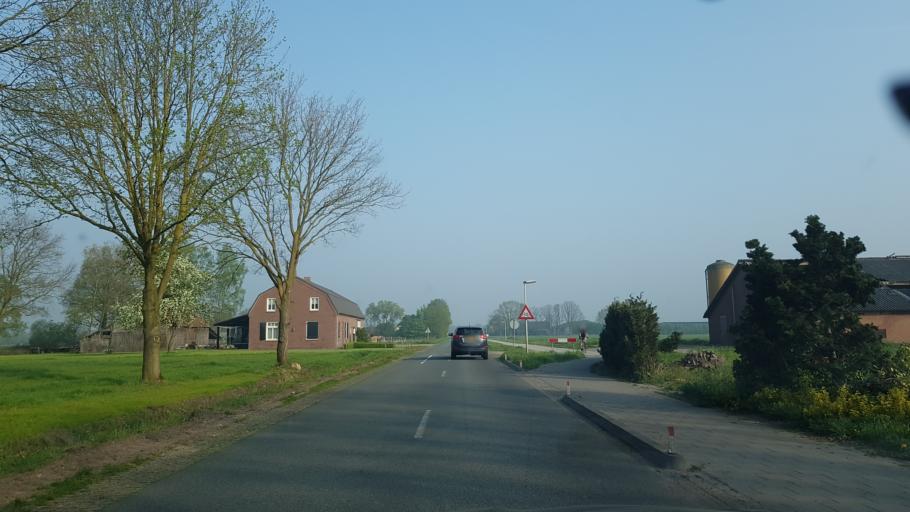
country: NL
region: Limburg
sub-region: Gemeente Nederweert
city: Nederweert
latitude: 51.3213
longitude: 5.6996
